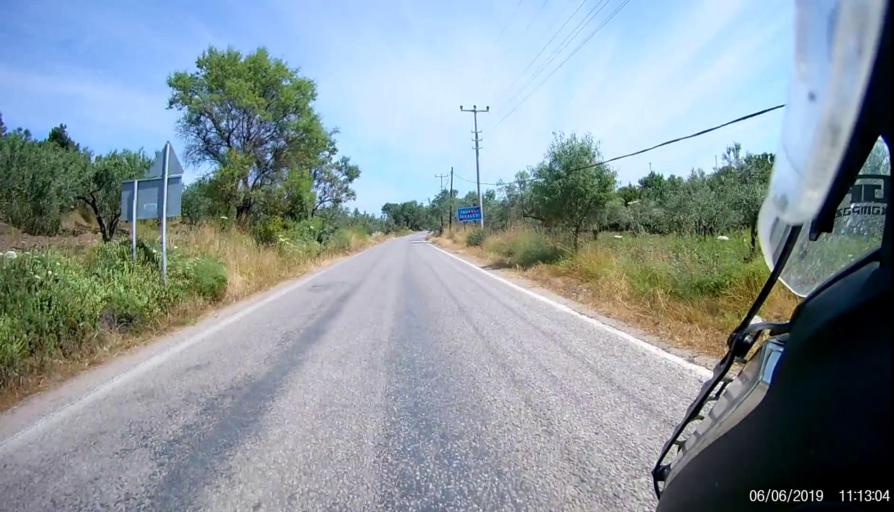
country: TR
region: Canakkale
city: Gulpinar
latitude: 39.6126
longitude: 26.1811
